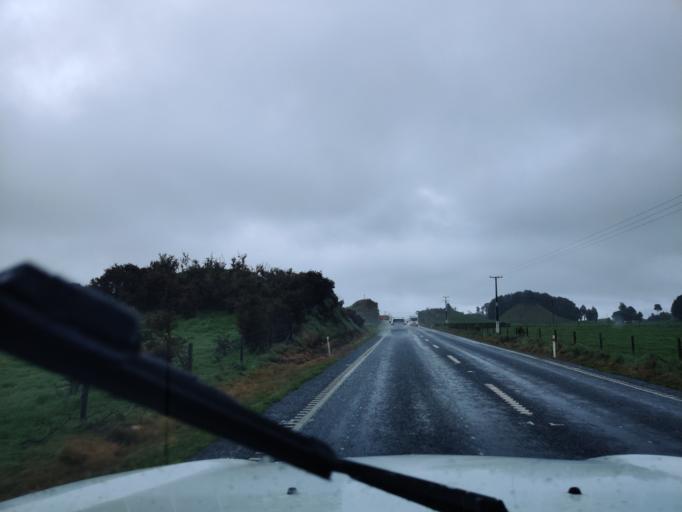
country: NZ
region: Bay of Plenty
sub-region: Rotorua District
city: Rotorua
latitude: -38.0469
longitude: 176.0712
